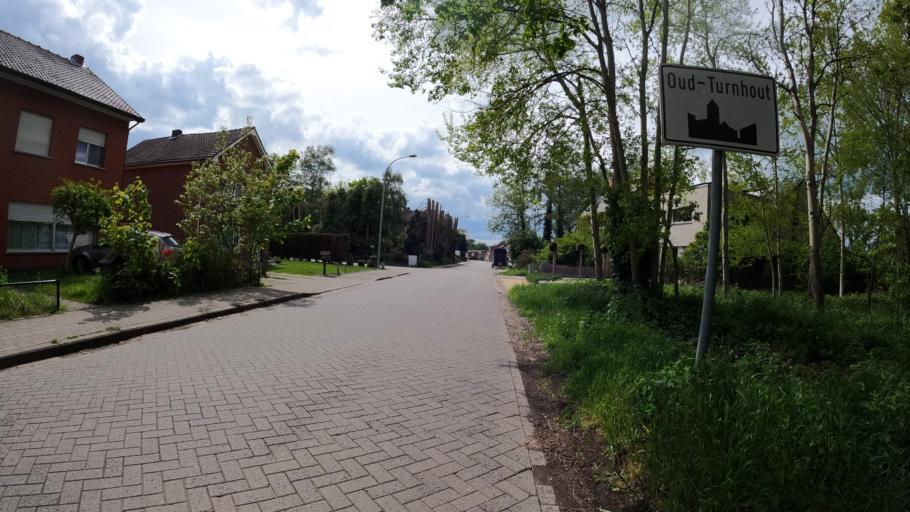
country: BE
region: Flanders
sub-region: Provincie Antwerpen
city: Oud-Turnhout
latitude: 51.3148
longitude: 4.9941
